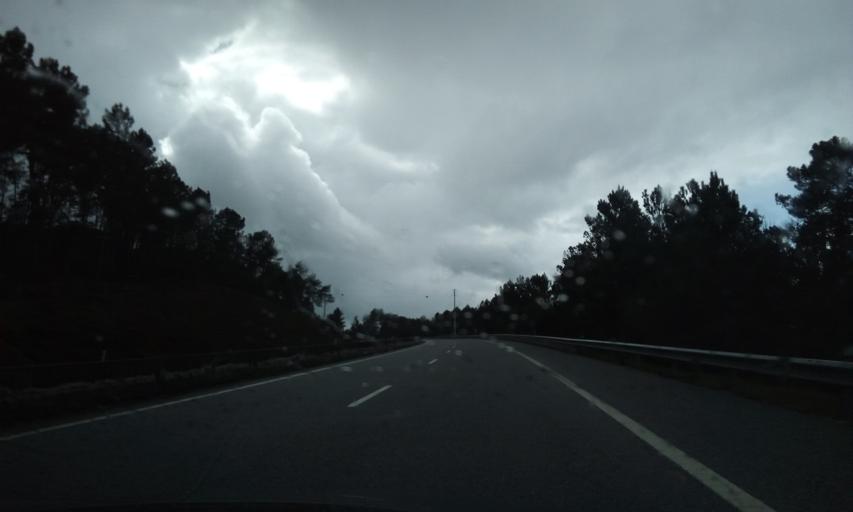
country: PT
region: Viseu
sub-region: Viseu
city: Viseu
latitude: 40.6285
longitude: -7.8997
